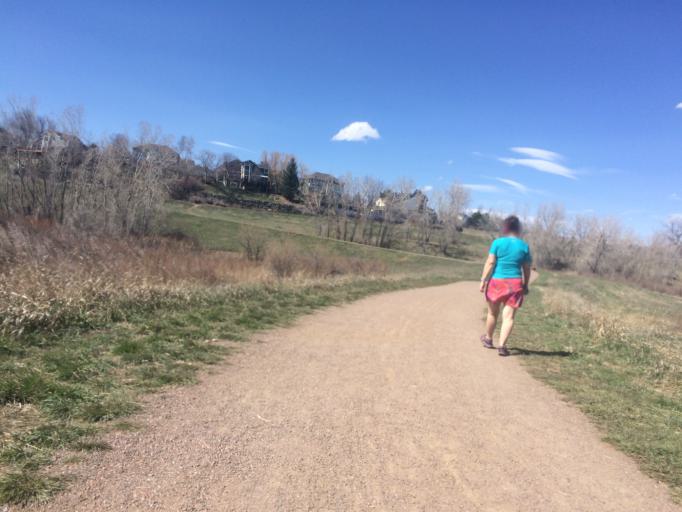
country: US
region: Colorado
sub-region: Boulder County
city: Louisville
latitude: 39.9824
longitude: -105.1478
